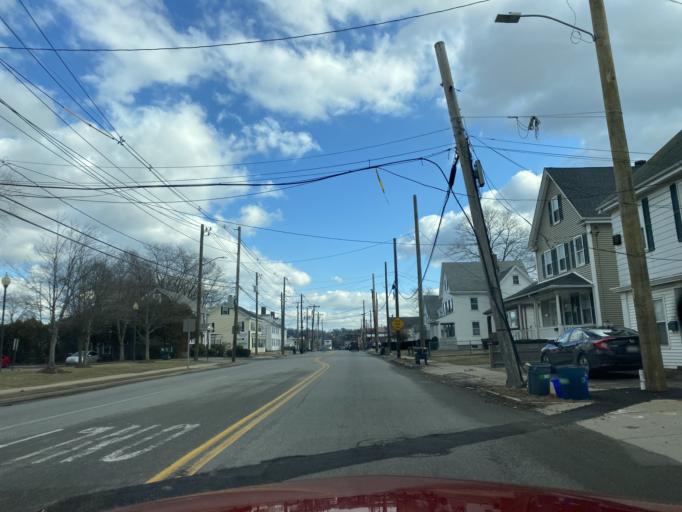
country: US
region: Massachusetts
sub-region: Middlesex County
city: Stoneham
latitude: 42.4798
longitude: -71.1238
